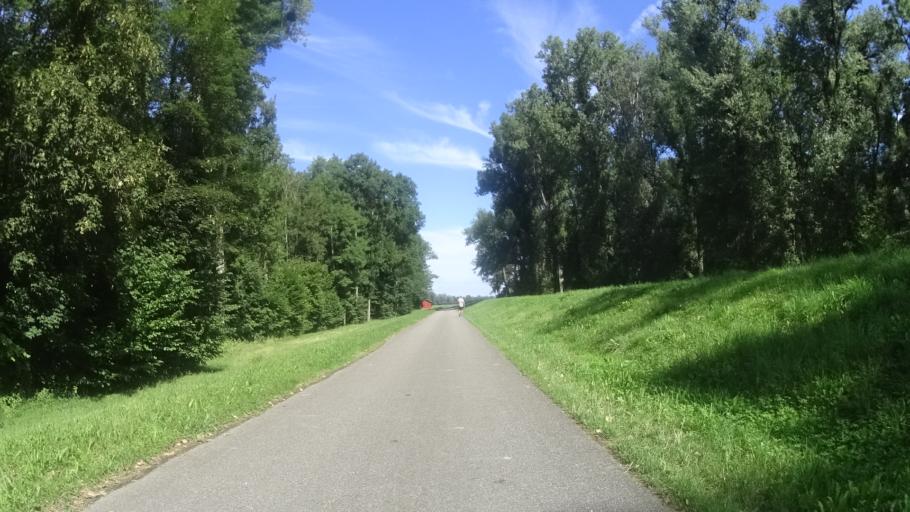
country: DE
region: Rheinland-Pfalz
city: Leimersheim
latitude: 49.1047
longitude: 8.3524
